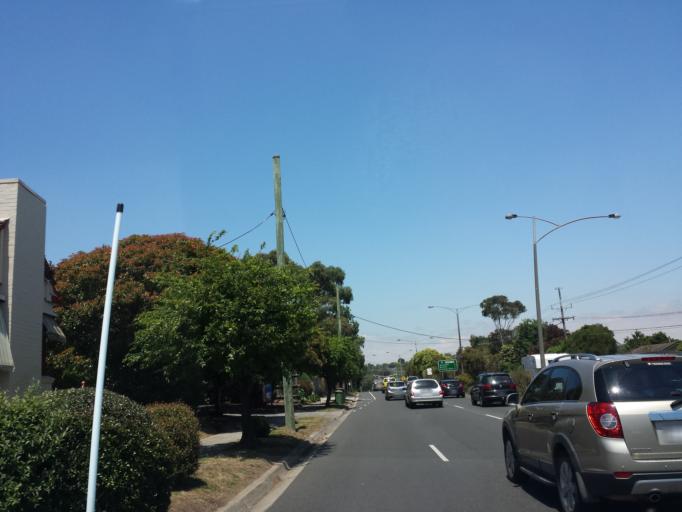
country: AU
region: Victoria
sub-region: Maroondah
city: Croydon North
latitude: -37.8001
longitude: 145.2898
